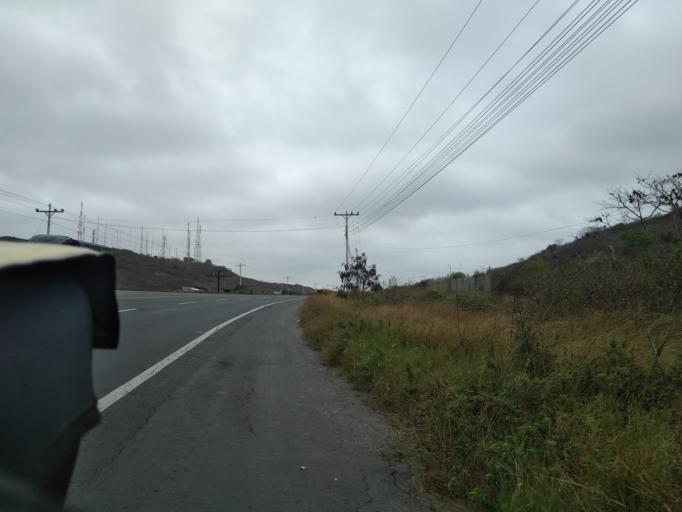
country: EC
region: Santa Elena
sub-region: Canton Santa Elena
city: Santa Elena
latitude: -2.2056
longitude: -80.8563
